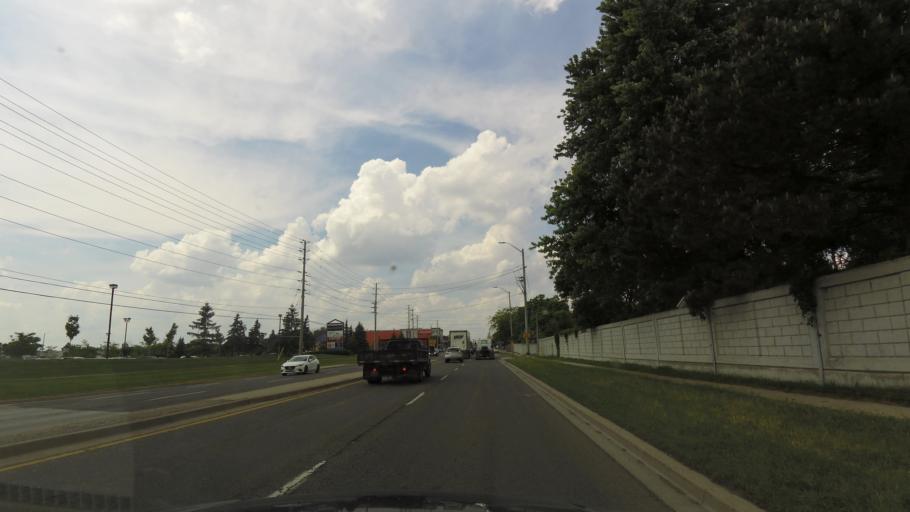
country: CA
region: Ontario
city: Mississauga
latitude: 43.5213
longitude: -79.6795
